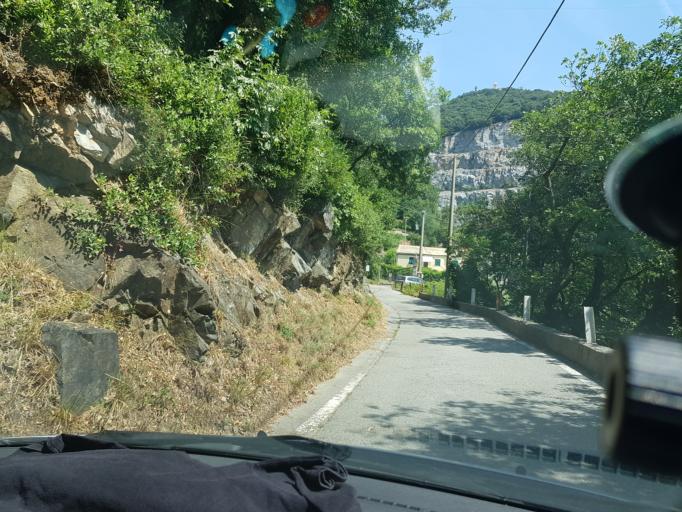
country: IT
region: Liguria
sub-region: Provincia di Genova
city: San Teodoro
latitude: 44.4366
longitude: 8.8449
